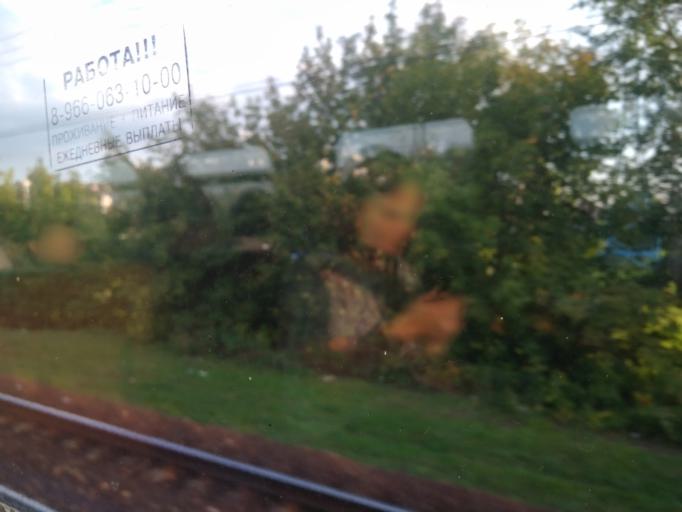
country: RU
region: Moscow
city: Zhulebino
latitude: 55.7073
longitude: 37.8435
